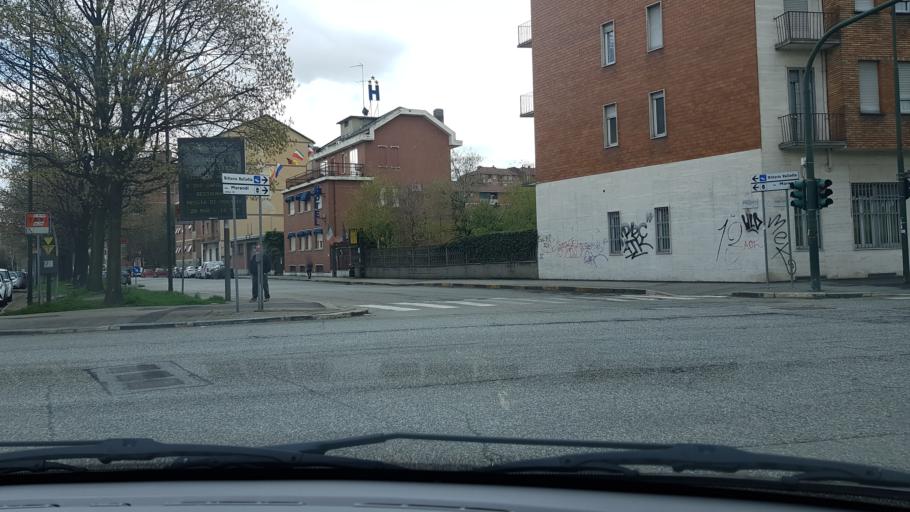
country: IT
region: Piedmont
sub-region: Provincia di Torino
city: Nichelino
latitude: 45.0162
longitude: 7.6280
